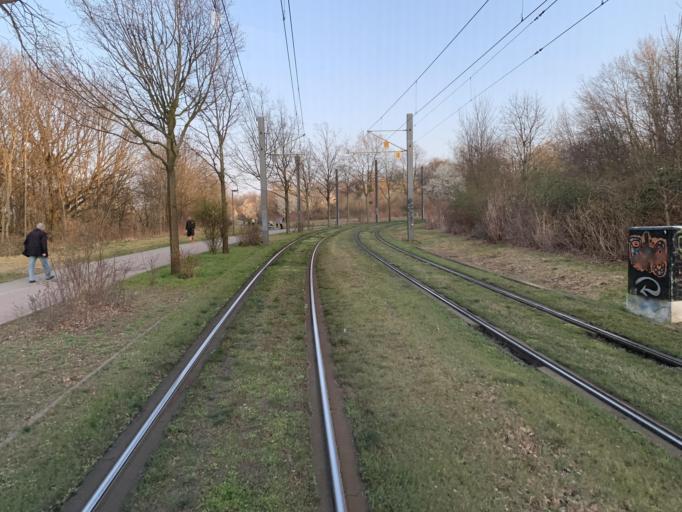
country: DE
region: Saxony
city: Bannewitz
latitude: 51.0231
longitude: 13.7195
